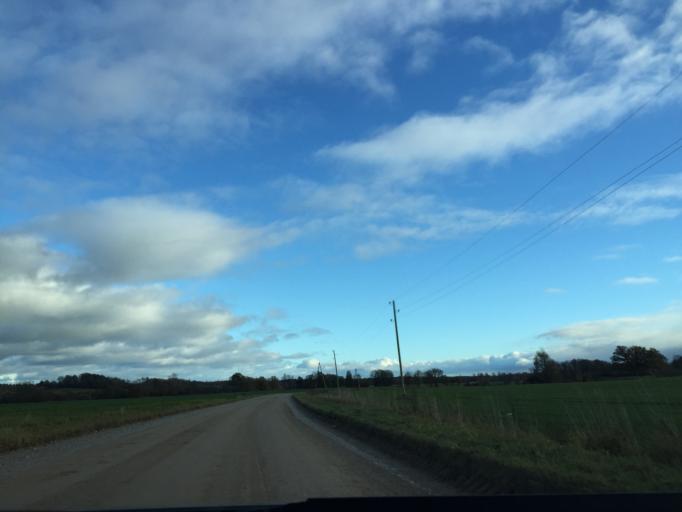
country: LV
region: Jaunpils
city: Jaunpils
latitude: 56.9196
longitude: 22.9571
